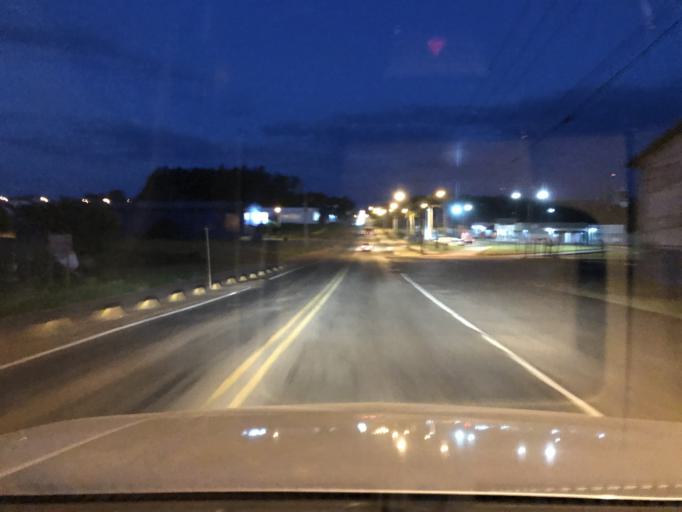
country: PY
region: Canindeyu
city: Salto del Guaira
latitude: -24.0868
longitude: -54.2425
